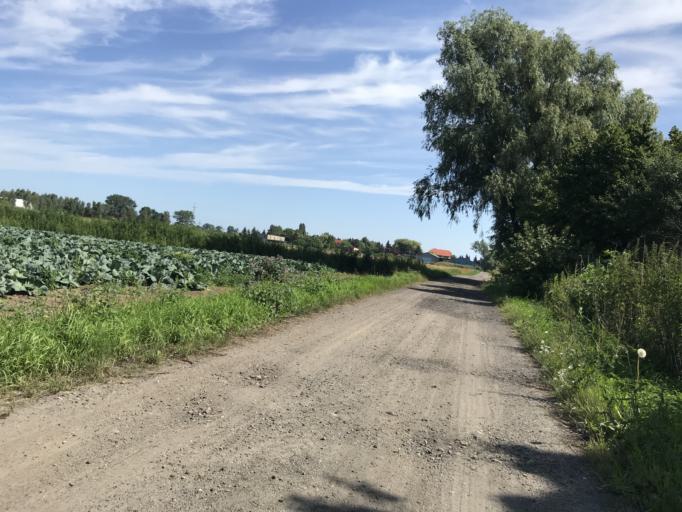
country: PL
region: Pomeranian Voivodeship
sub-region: Gdansk
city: Gdansk
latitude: 54.3275
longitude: 18.6780
